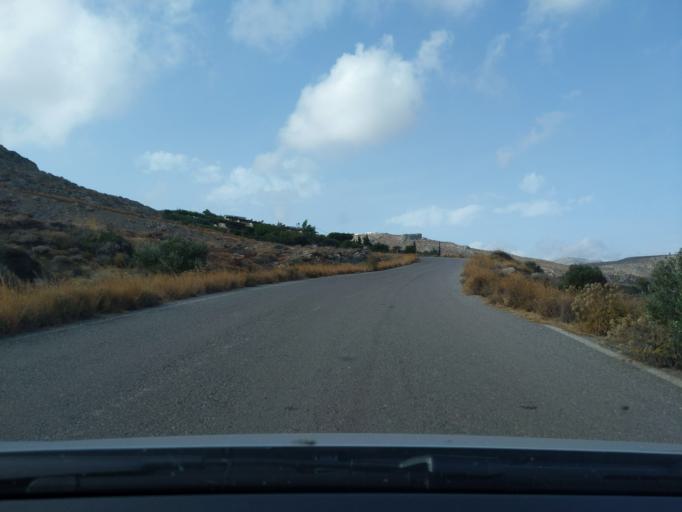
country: GR
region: Crete
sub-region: Nomos Lasithiou
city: Palekastro
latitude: 35.0944
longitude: 26.2621
